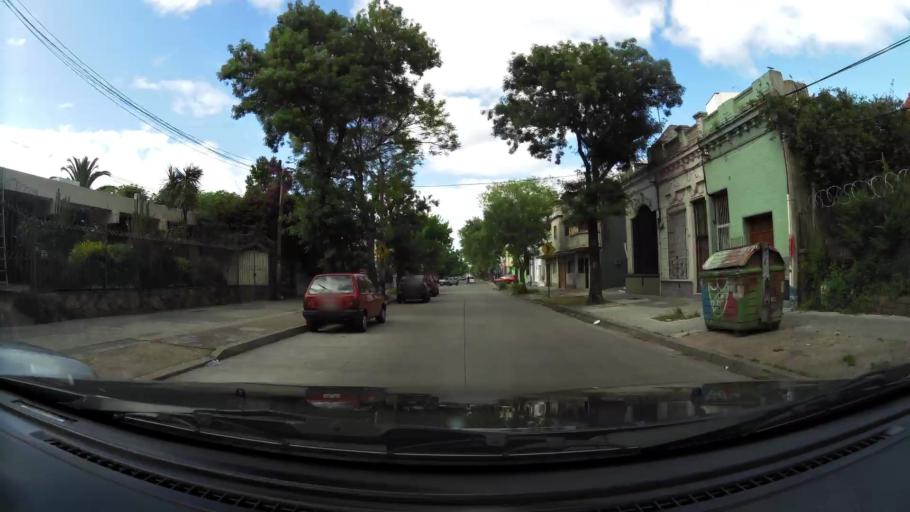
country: UY
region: Montevideo
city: Montevideo
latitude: -34.8838
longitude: -56.1570
